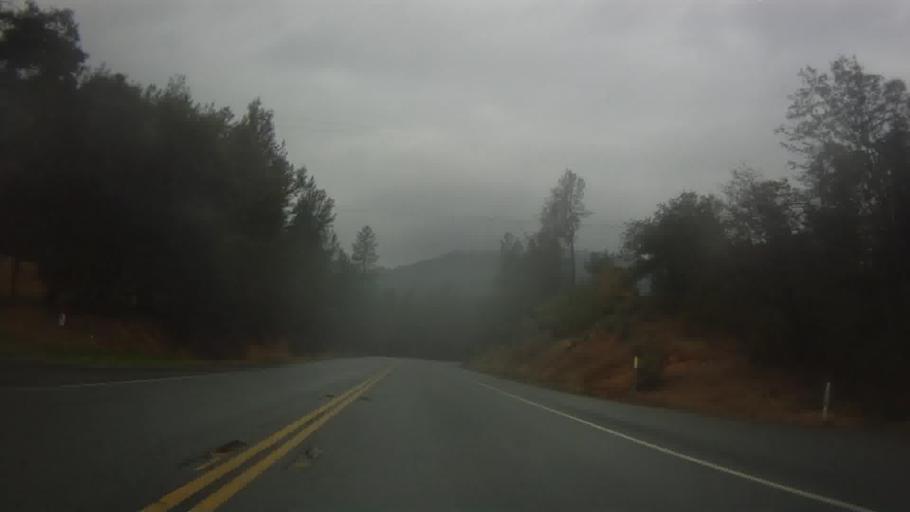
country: US
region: California
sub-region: Shasta County
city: Shasta
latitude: 40.5909
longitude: -122.4775
